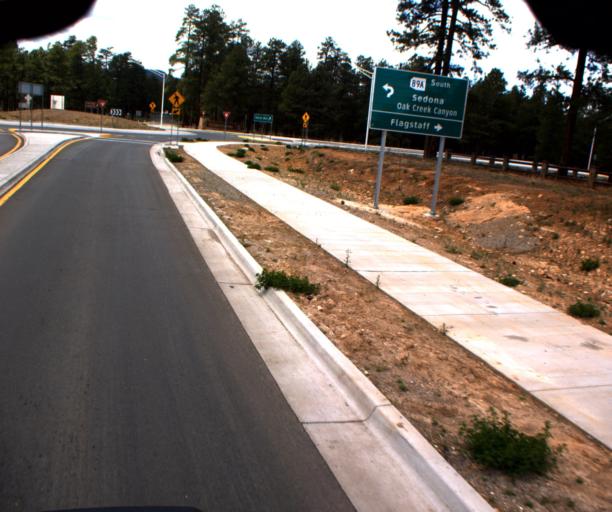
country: US
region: Arizona
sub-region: Coconino County
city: Kachina Village
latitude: 35.1400
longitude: -111.6861
